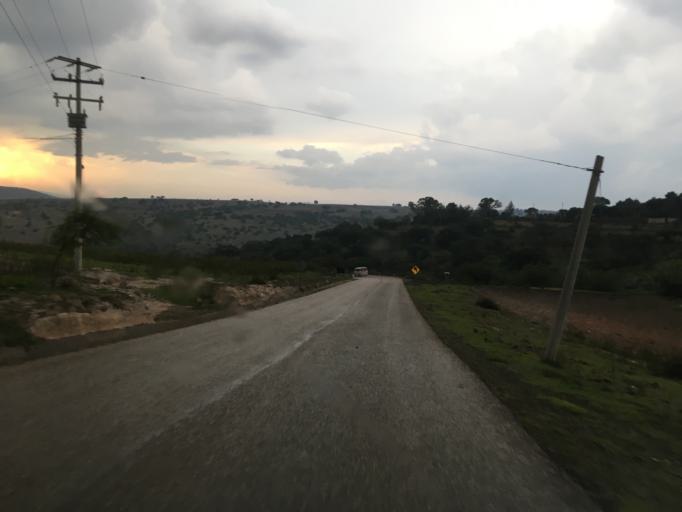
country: MX
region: Oaxaca
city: Santiago Tilantongo
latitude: 17.2881
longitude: -97.2795
